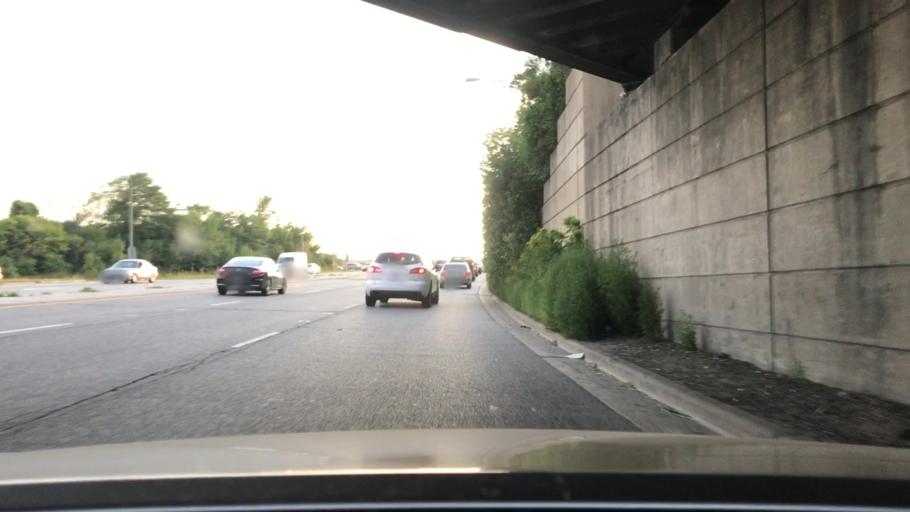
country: US
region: Illinois
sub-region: Cook County
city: Hickory Hills
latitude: 41.7190
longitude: -87.8020
